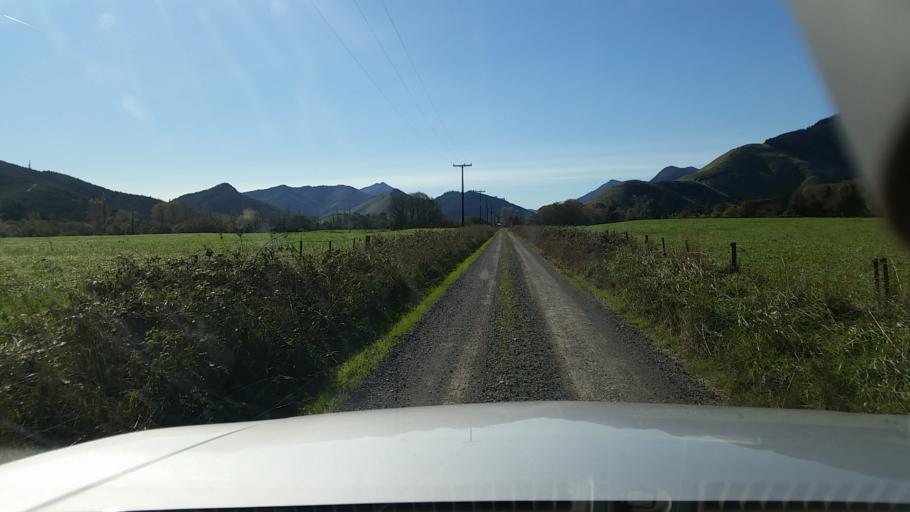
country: NZ
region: Nelson
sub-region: Nelson City
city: Nelson
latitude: -41.2587
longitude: 173.5816
